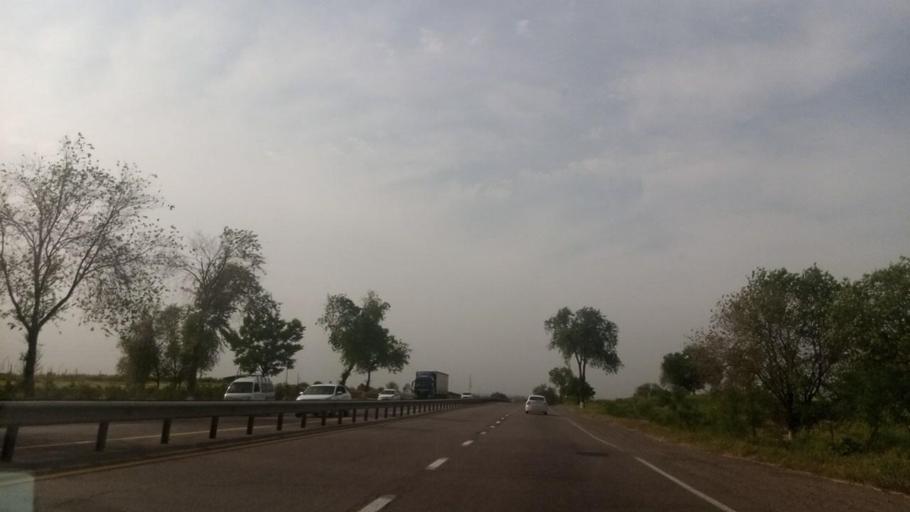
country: UZ
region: Toshkent
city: Tuytepa
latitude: 41.1073
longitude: 69.4513
